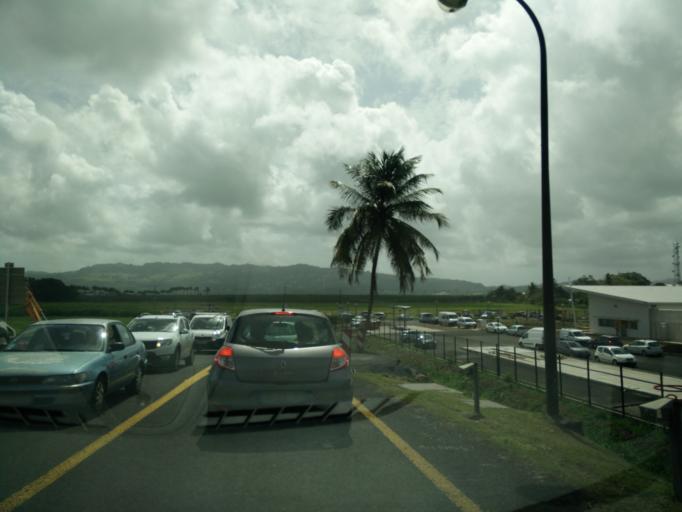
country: MQ
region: Martinique
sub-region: Martinique
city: Le Lamentin
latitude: 14.5992
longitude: -60.9989
